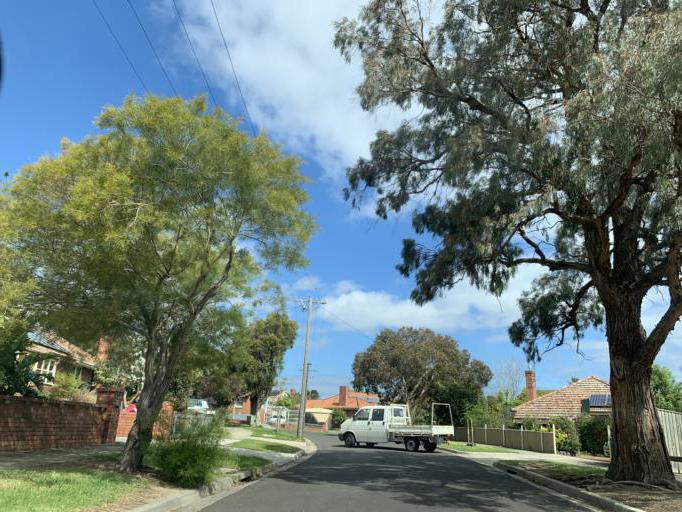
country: AU
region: Victoria
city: Thornbury
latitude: -37.7334
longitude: 144.9846
